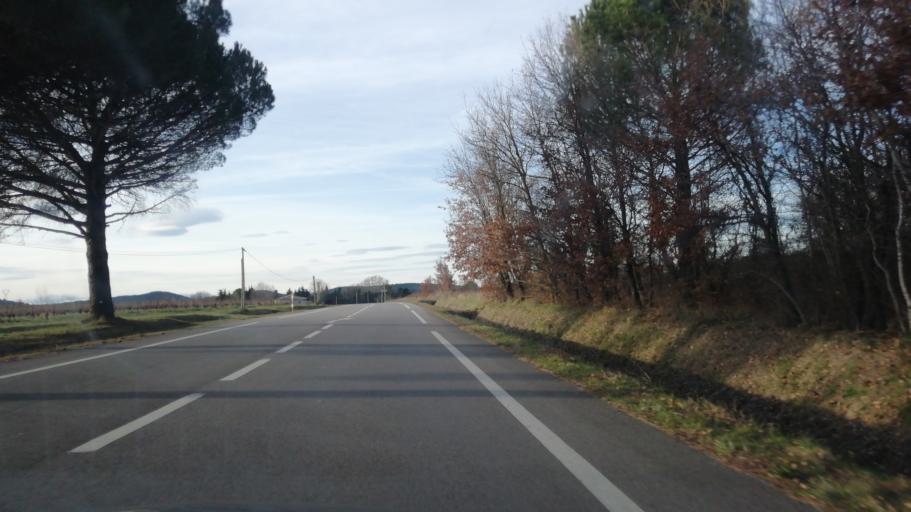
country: FR
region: Languedoc-Roussillon
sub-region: Departement du Gard
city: Saint-Mamert-du-Gard
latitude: 43.8586
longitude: 4.1703
